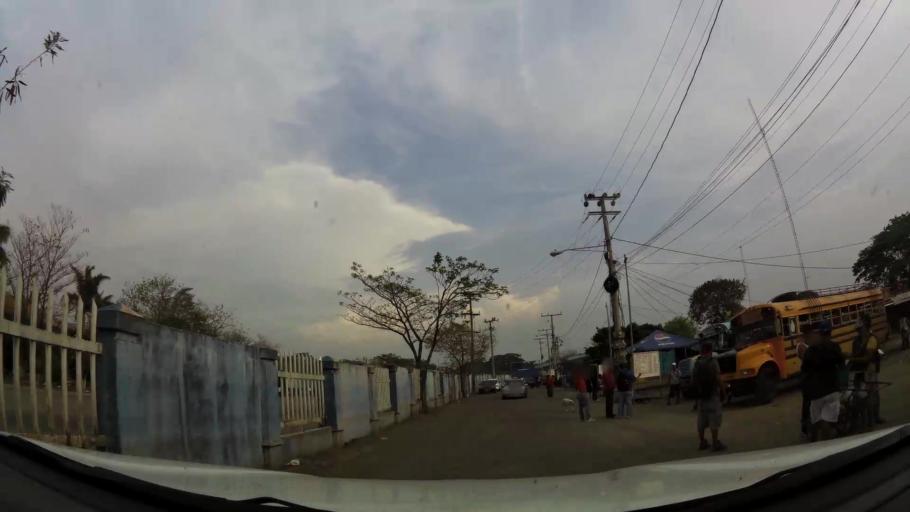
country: NI
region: Rivas
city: Cardenas
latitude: 11.2181
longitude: -85.6135
